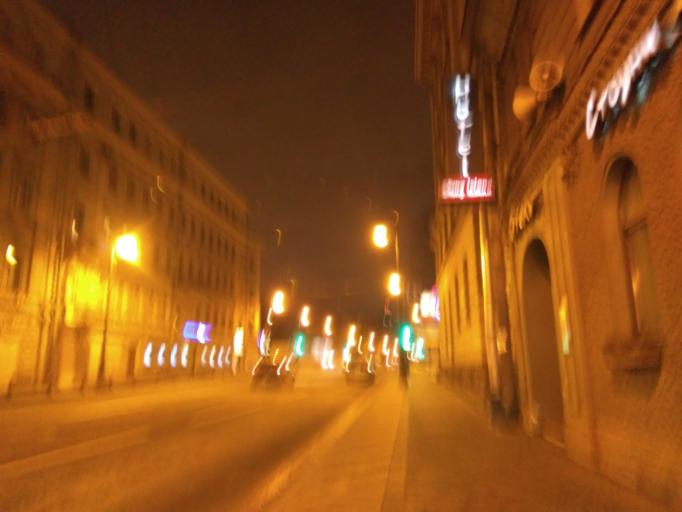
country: RU
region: St.-Petersburg
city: Petrogradka
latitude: 59.9689
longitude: 30.3083
